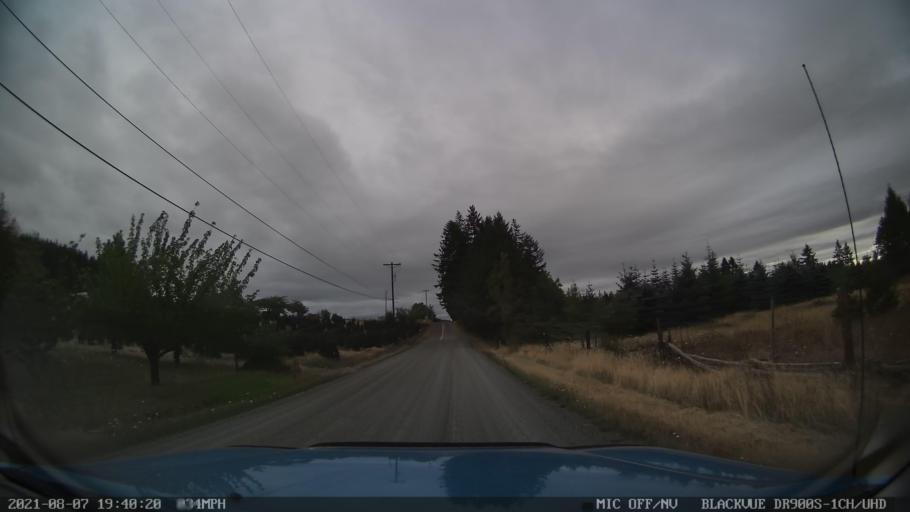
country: US
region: Oregon
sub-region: Marion County
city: Silverton
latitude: 44.9294
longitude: -122.6568
